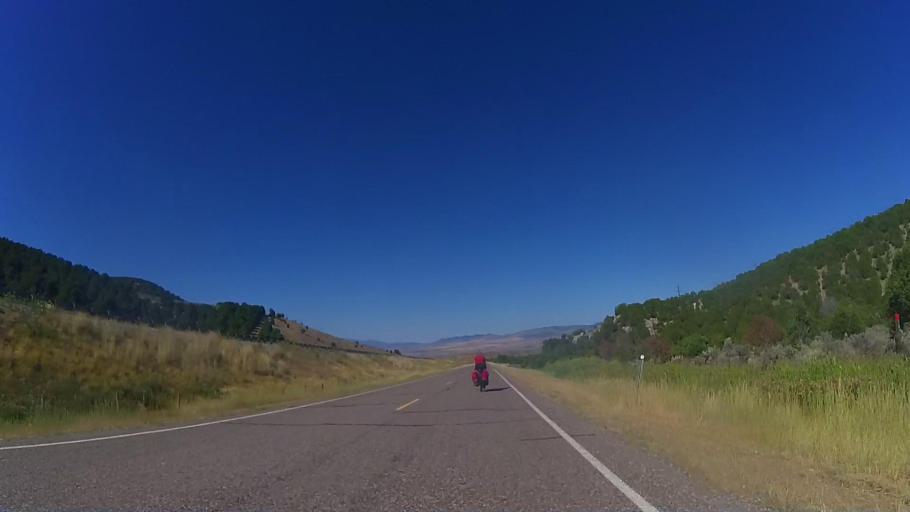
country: US
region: Idaho
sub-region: Oneida County
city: Malad City
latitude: 42.3608
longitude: -112.2171
